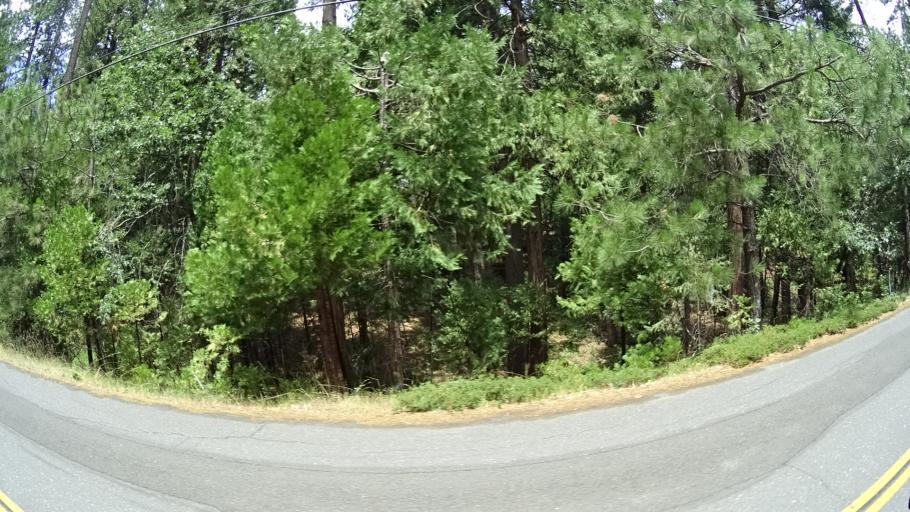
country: US
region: California
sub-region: Calaveras County
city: Arnold
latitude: 38.2375
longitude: -120.3517
